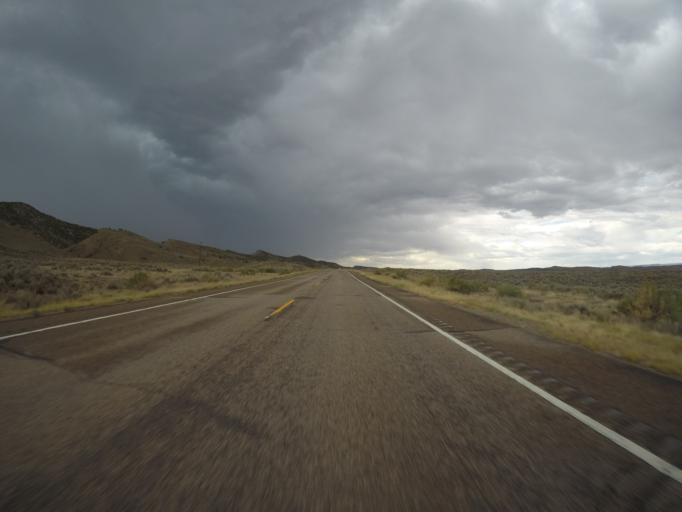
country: US
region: Colorado
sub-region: Rio Blanco County
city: Rangely
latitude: 40.2487
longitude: -108.8738
